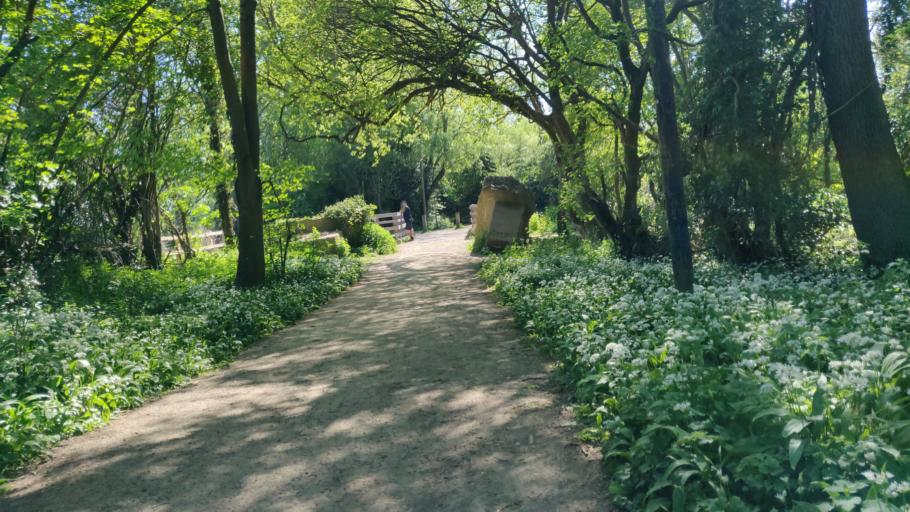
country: GB
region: England
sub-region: West Sussex
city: Southwater
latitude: 51.0612
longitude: -0.3698
